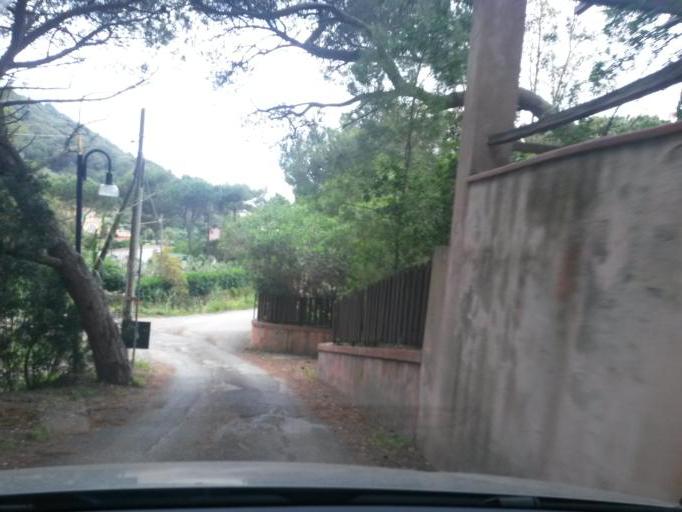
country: IT
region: Tuscany
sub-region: Provincia di Livorno
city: Rio nell'Elba
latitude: 42.8321
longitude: 10.3881
